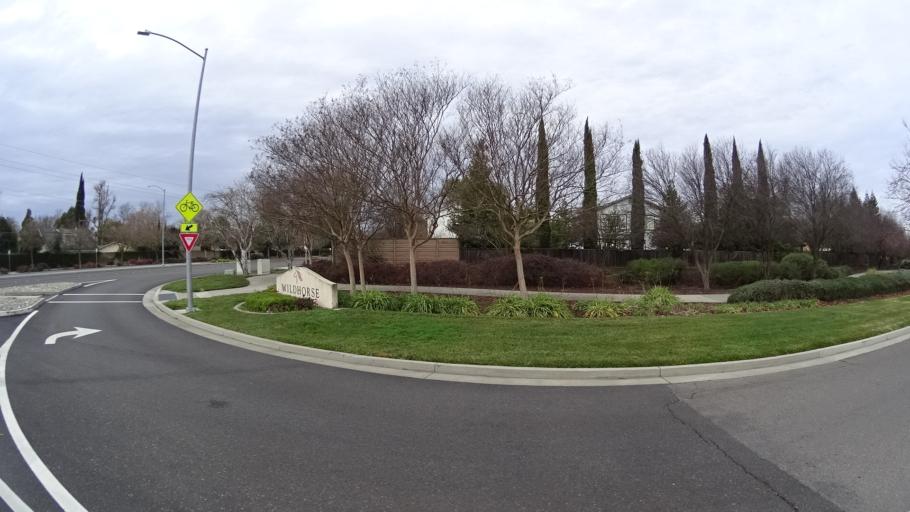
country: US
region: California
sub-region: Yolo County
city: Davis
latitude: 38.5638
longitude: -121.7177
